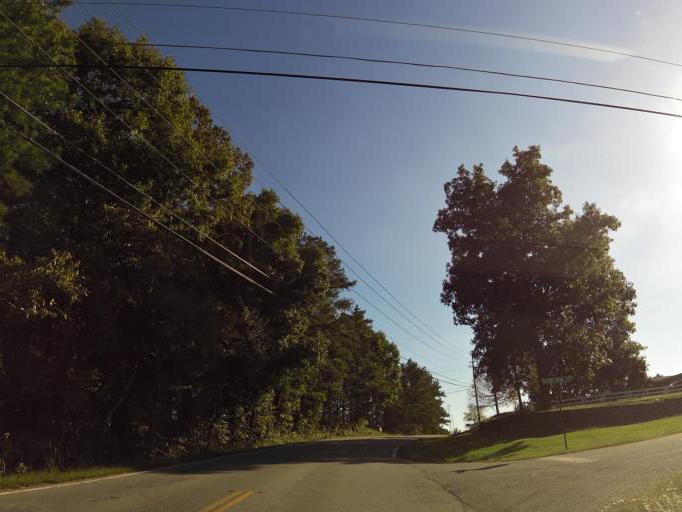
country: US
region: Georgia
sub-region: Cobb County
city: Acworth
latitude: 34.1209
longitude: -84.6799
